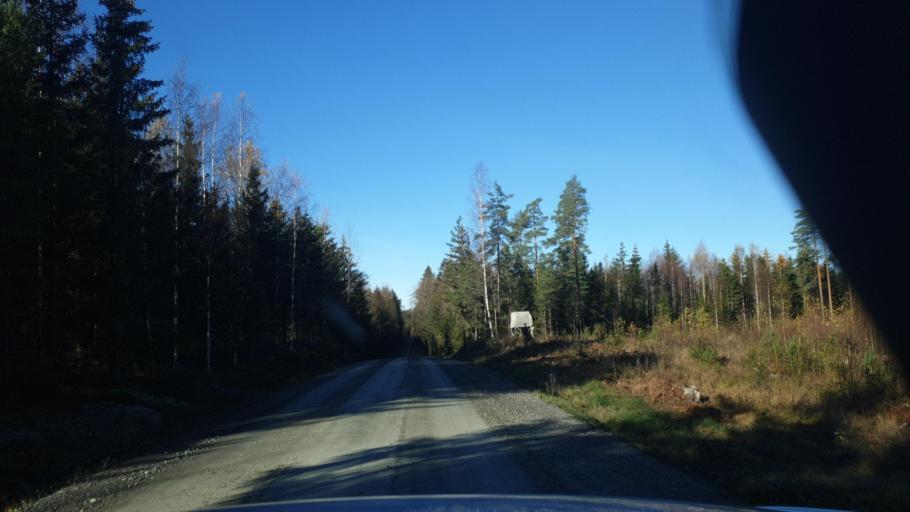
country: SE
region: Vaermland
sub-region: Karlstads Kommun
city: Valberg
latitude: 59.4494
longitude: 13.1076
